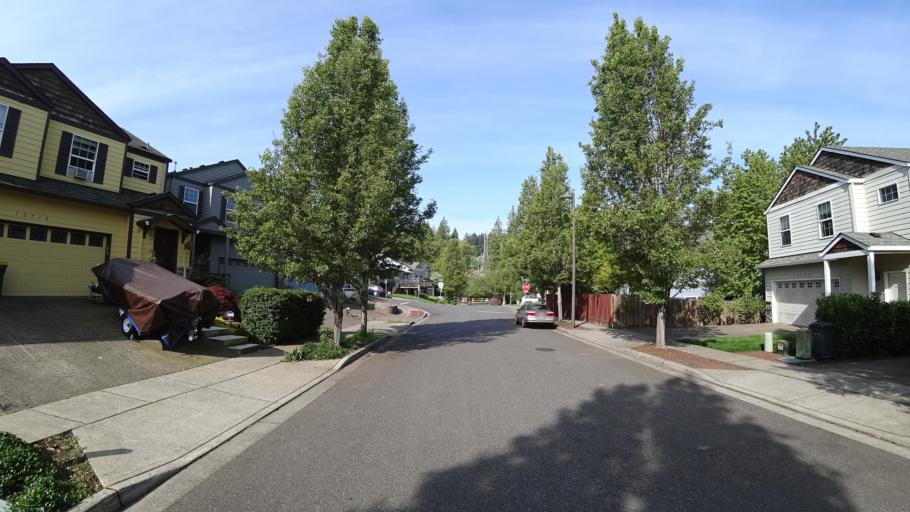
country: US
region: Oregon
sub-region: Washington County
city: Beaverton
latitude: 45.4536
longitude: -122.8385
